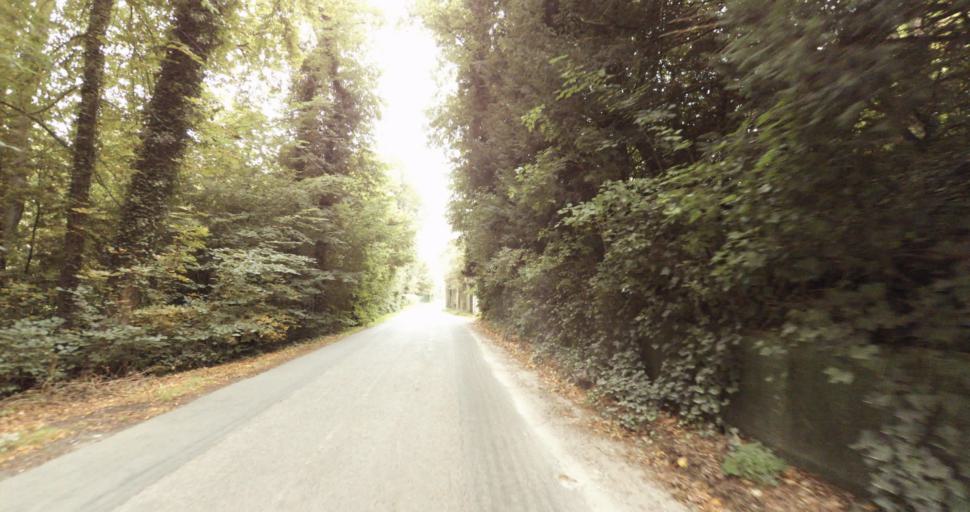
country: FR
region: Centre
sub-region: Departement d'Eure-et-Loir
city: Vert-en-Drouais
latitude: 48.7664
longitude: 1.3079
